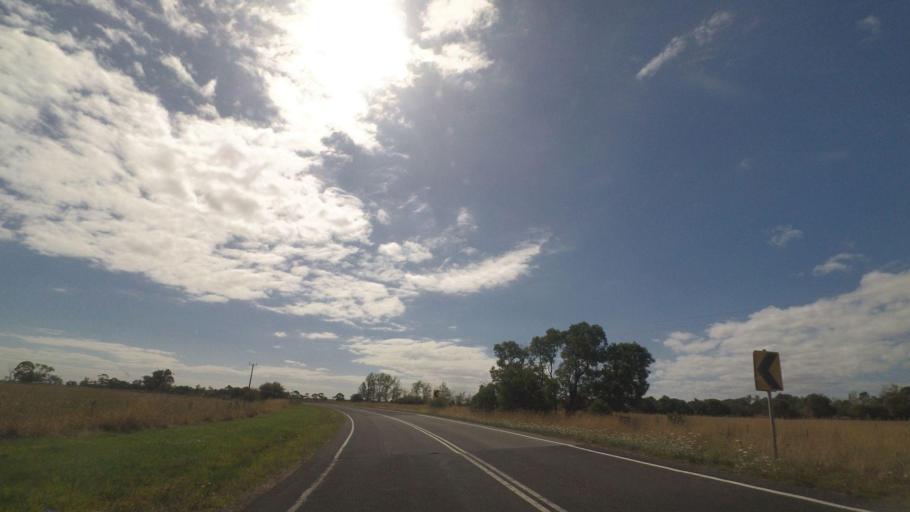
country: AU
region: Victoria
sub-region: Cardinia
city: Garfield
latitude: -38.2143
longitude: 145.6413
